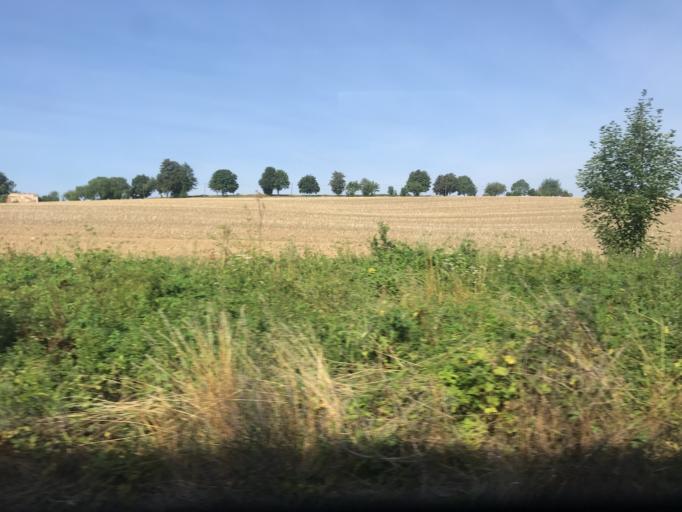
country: CZ
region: Central Bohemia
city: Votice
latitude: 49.5511
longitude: 14.6157
